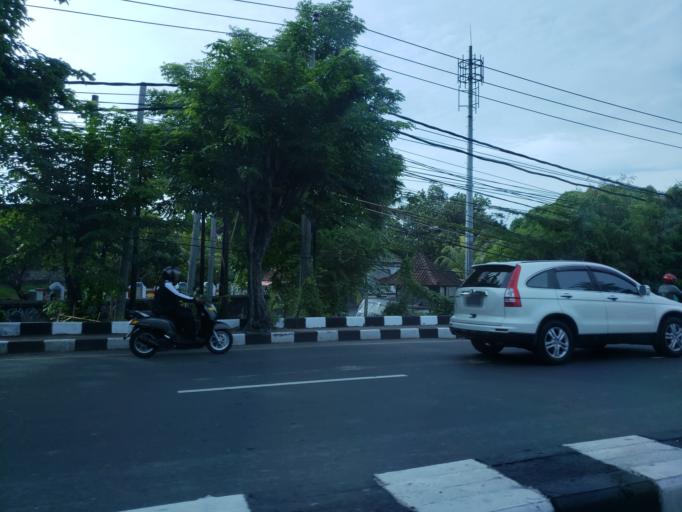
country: ID
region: Bali
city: Jabajero
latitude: -8.7288
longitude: 115.1795
